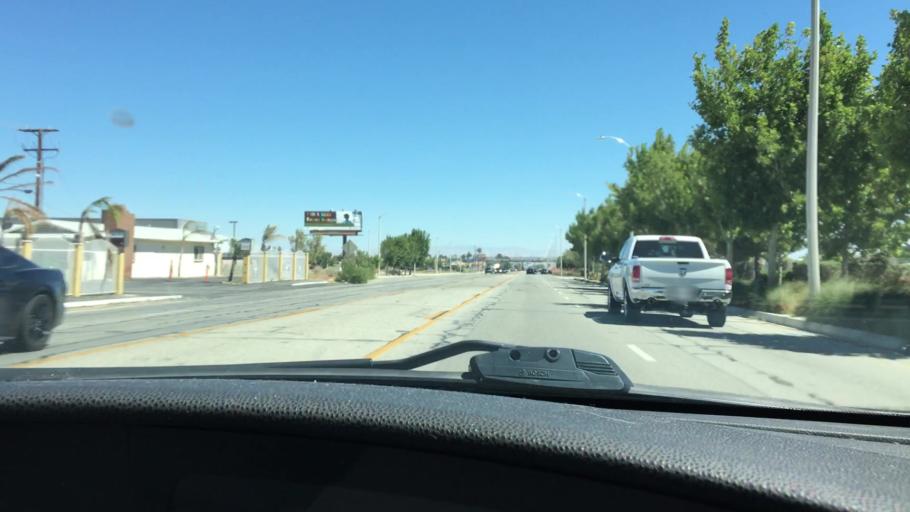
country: US
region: California
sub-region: Los Angeles County
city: Lancaster
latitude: 34.6541
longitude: -118.1295
